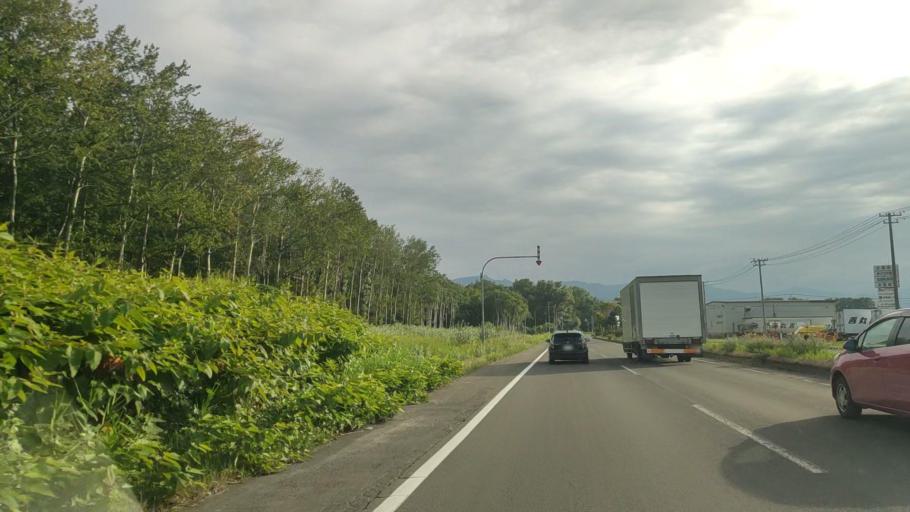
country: JP
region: Hokkaido
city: Ishikari
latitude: 43.1614
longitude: 141.2832
